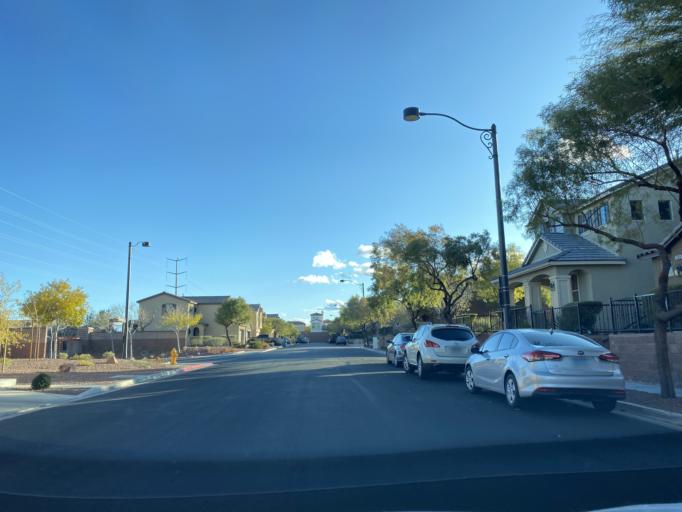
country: US
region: Nevada
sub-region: Clark County
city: Summerlin South
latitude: 36.2977
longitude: -115.3295
